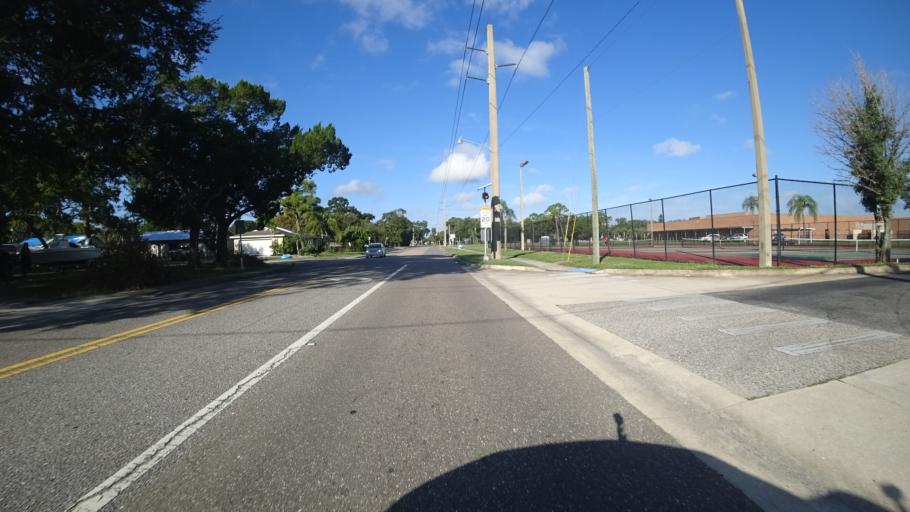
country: US
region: Florida
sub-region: Manatee County
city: West Bradenton
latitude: 27.4921
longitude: -82.6019
